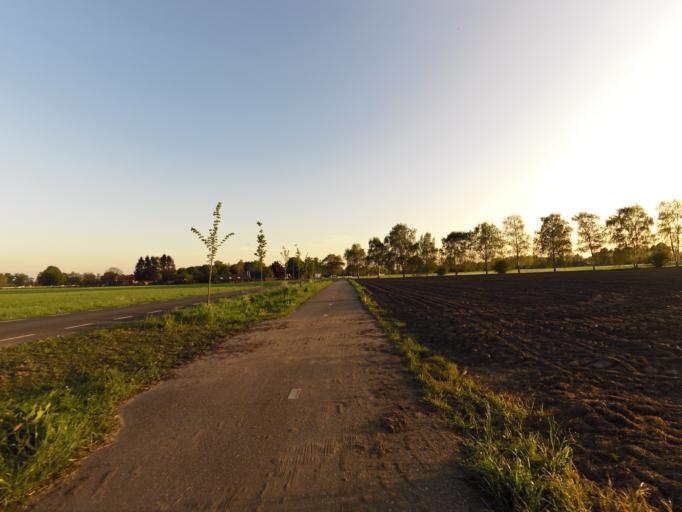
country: NL
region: Gelderland
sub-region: Oude IJsselstreek
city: Varsseveld
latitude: 51.9081
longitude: 6.4632
